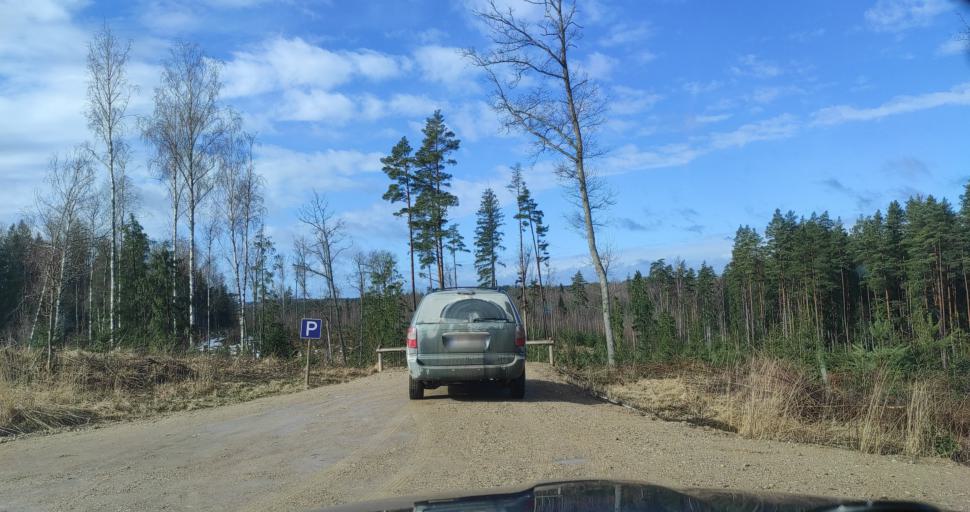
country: LV
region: Tukuma Rajons
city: Tukums
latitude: 57.1119
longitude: 23.0439
